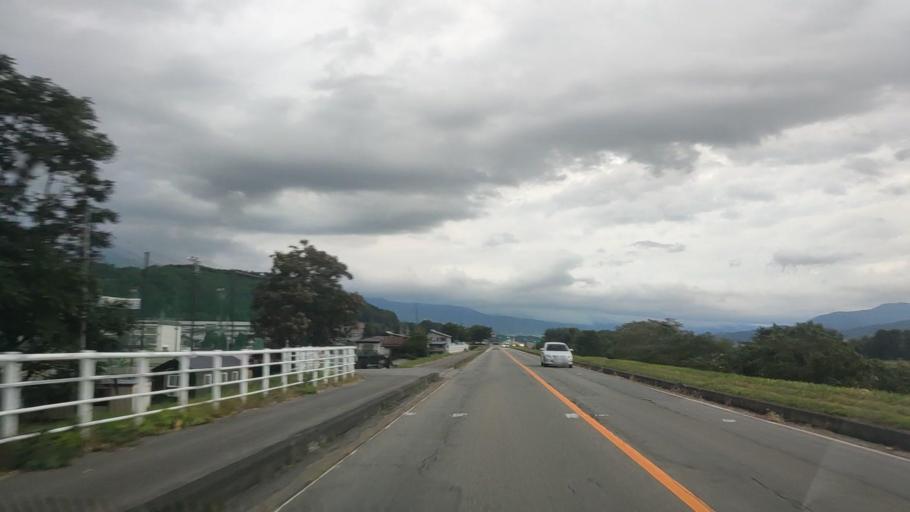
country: JP
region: Nagano
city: Iiyama
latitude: 36.8569
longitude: 138.3683
